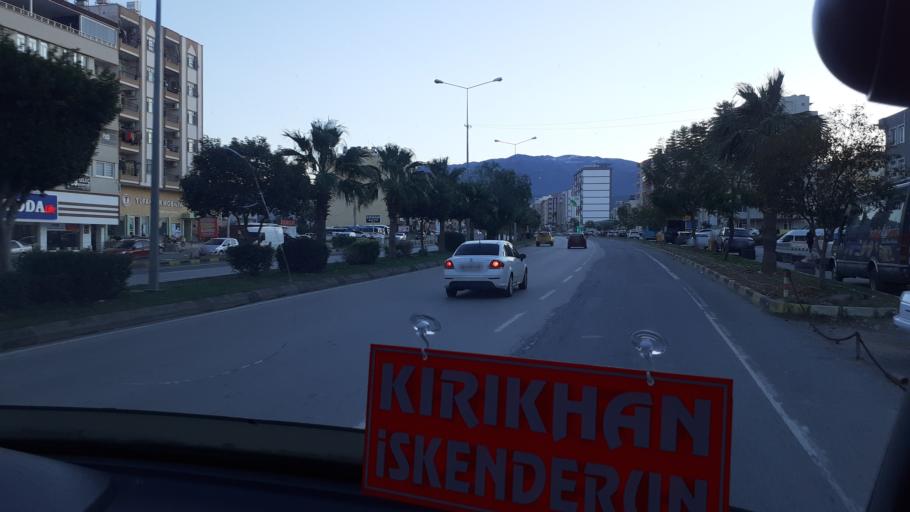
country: TR
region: Hatay
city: Iskenderun
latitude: 36.5699
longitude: 36.1579
